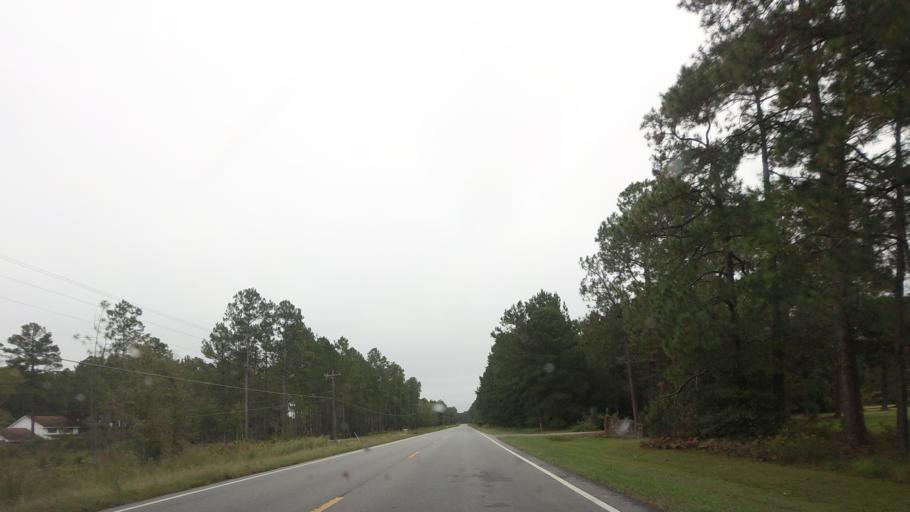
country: US
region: Georgia
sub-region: Berrien County
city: Nashville
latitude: 31.2457
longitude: -83.2429
